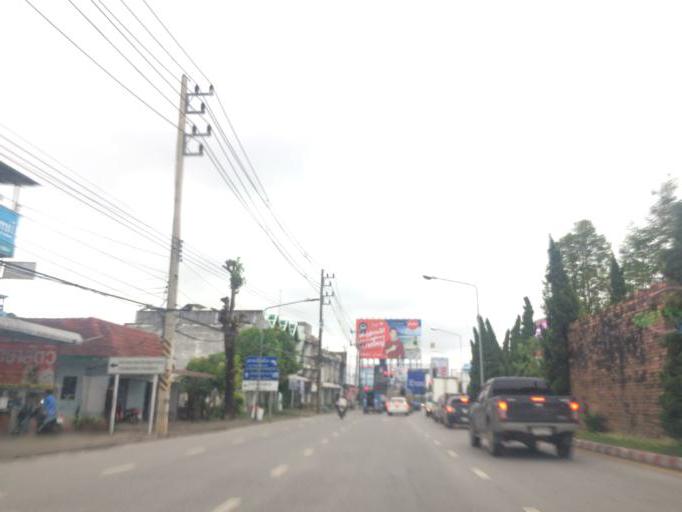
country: TH
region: Chiang Rai
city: Chiang Rai
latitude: 19.9092
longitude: 99.8404
